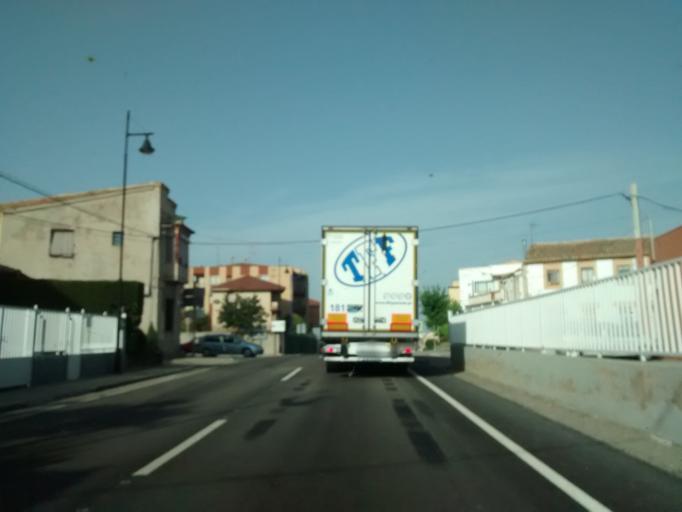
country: ES
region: Aragon
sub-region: Provincia de Zaragoza
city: Borja
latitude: 41.8309
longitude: -1.5362
